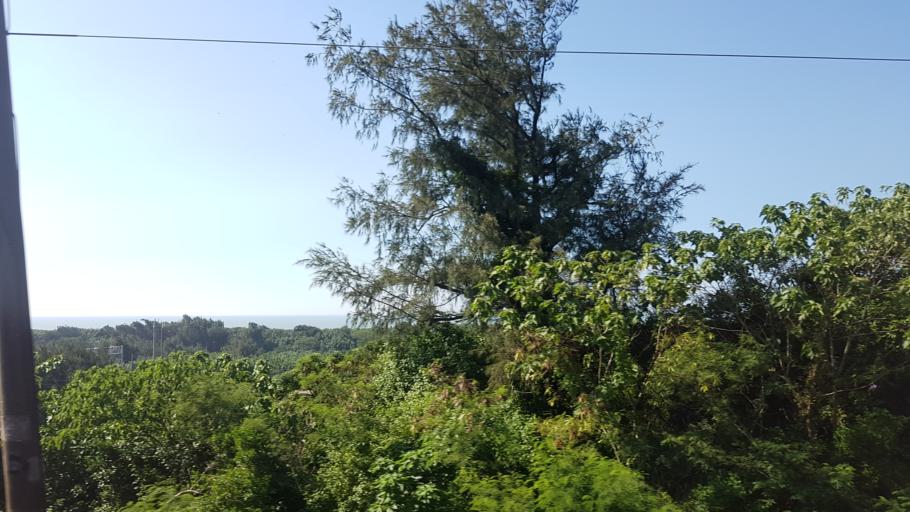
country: TW
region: Taiwan
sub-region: Hsinchu
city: Hsinchu
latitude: 24.7270
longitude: 120.8748
